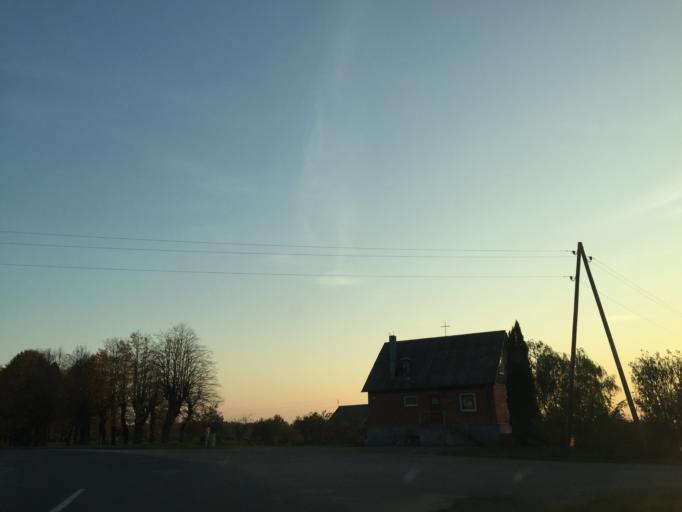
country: LV
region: Priekule
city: Priekule
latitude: 56.3673
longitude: 21.6029
